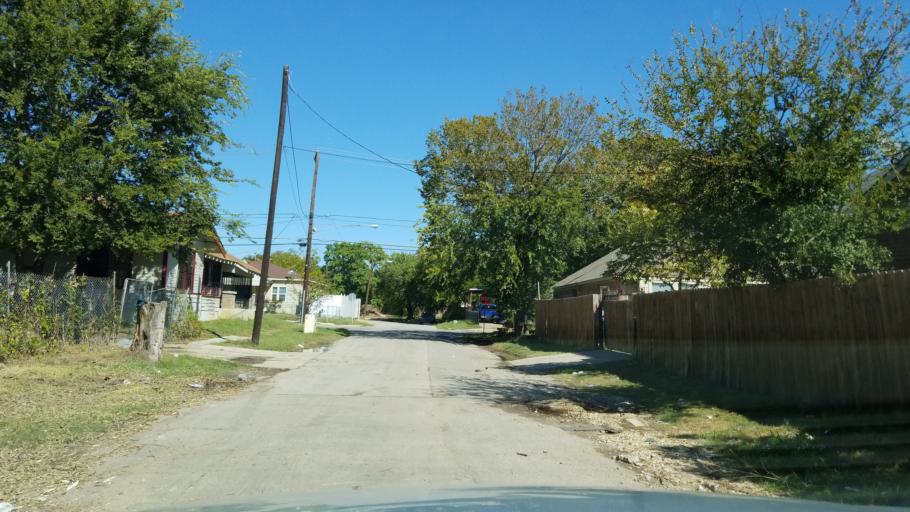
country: US
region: Texas
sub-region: Dallas County
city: Dallas
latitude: 32.7849
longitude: -96.7529
